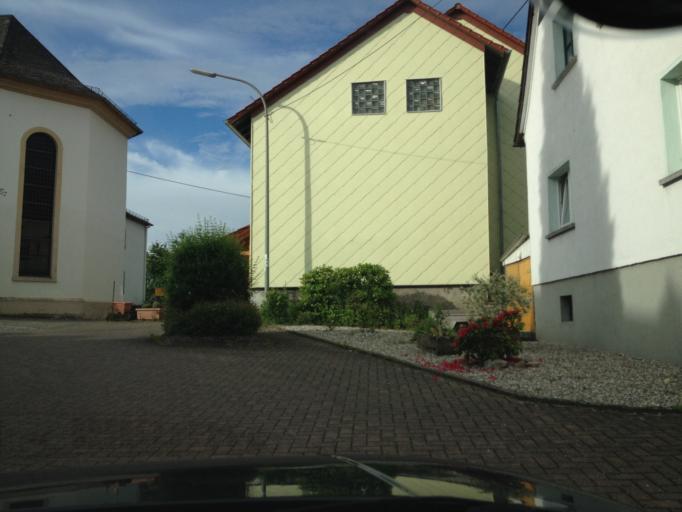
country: DE
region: Saarland
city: Marpingen
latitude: 49.4708
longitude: 7.0687
